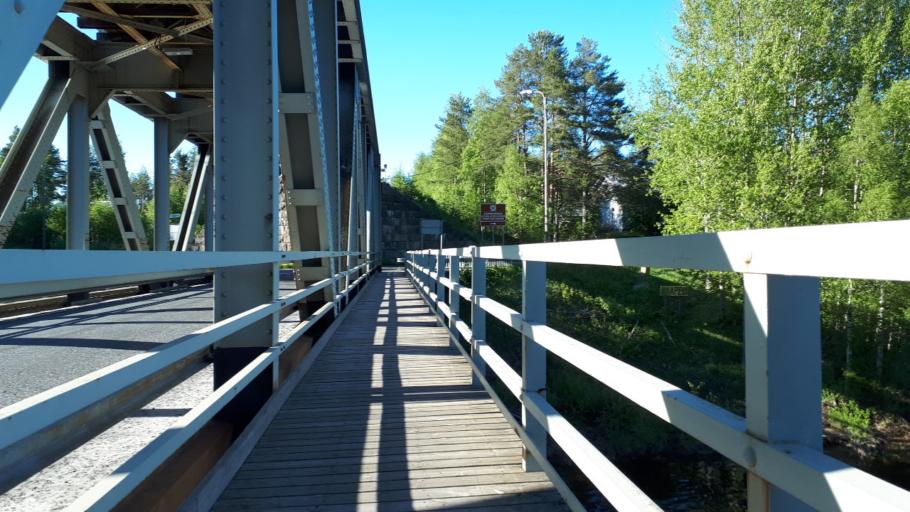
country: FI
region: Northern Ostrobothnia
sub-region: Oulunkaari
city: Ii
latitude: 65.3218
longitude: 25.4424
